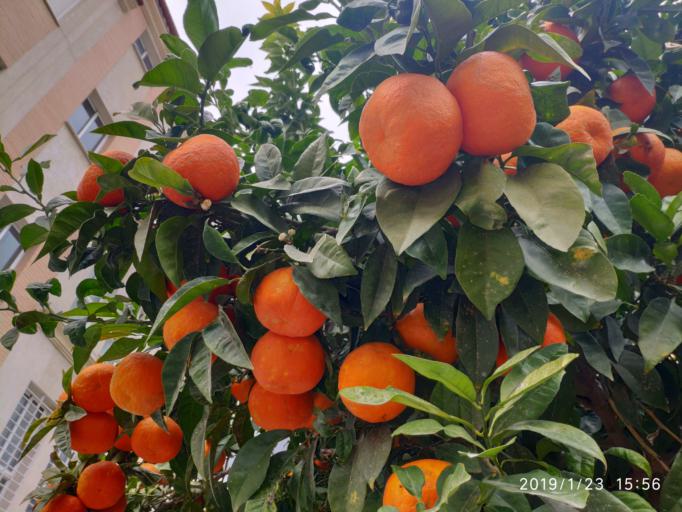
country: ES
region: Andalusia
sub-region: Provincia de Malaga
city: Malaga
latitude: 36.7254
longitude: -4.4235
